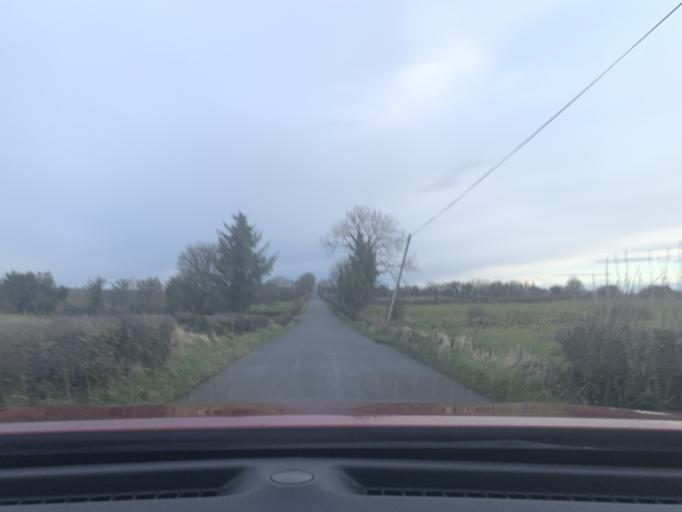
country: IE
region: Connaught
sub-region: Roscommon
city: Ballaghaderreen
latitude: 53.8723
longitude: -8.5575
